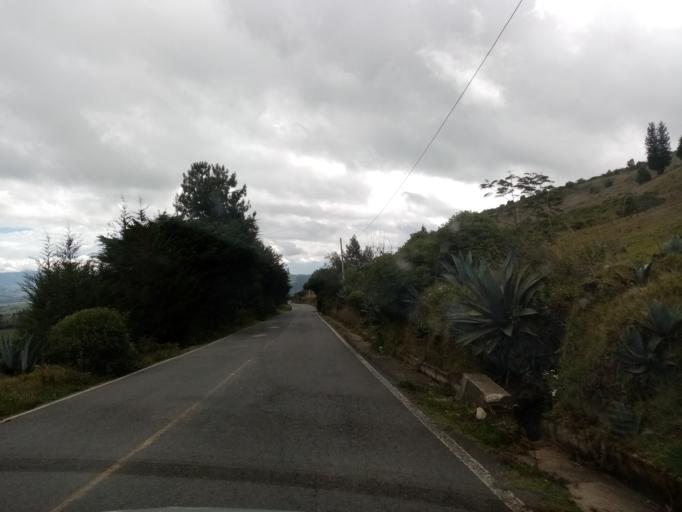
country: CO
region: Boyaca
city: Siachoque
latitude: 5.5685
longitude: -73.2753
